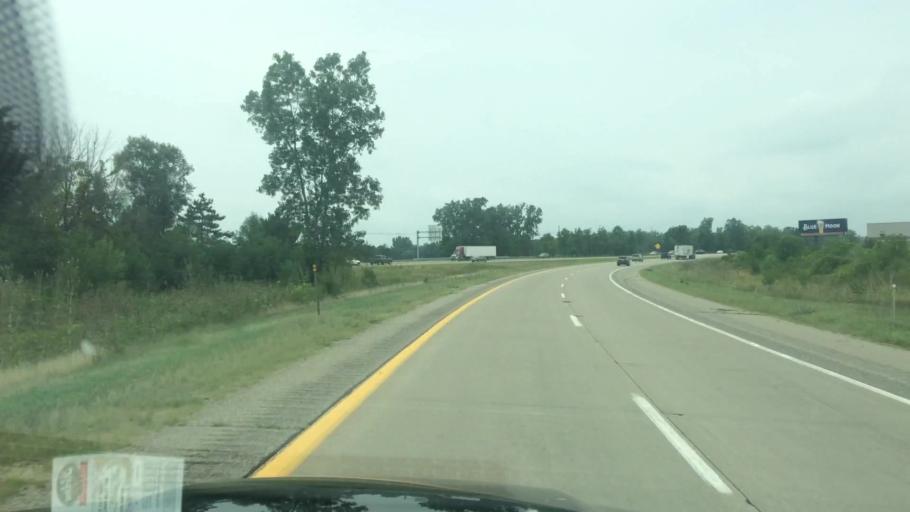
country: US
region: Michigan
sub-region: Eaton County
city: Dimondale
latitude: 42.6984
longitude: -84.6684
